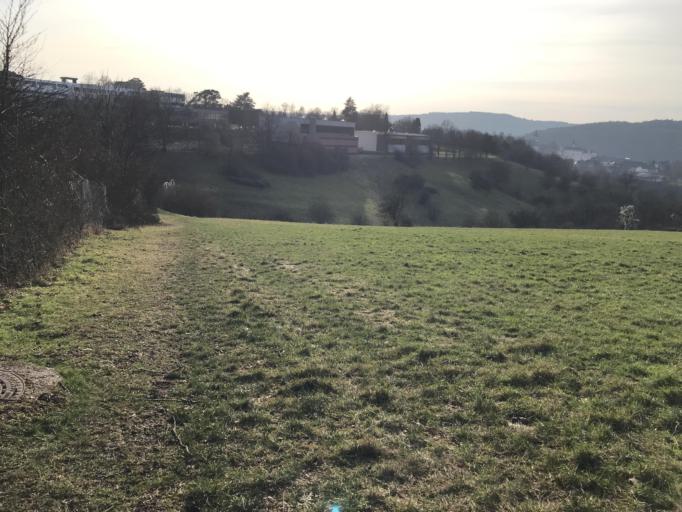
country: DE
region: Hesse
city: Weilburg
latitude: 50.4894
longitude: 8.2781
